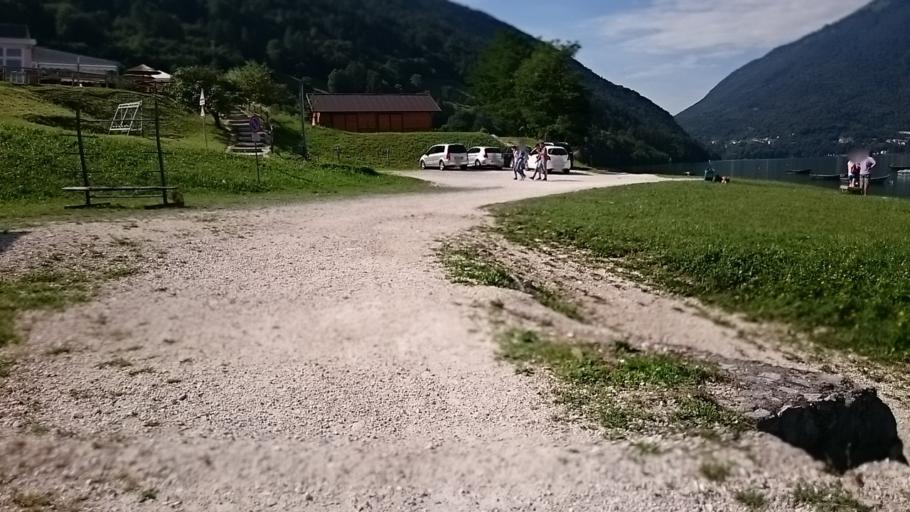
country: IT
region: Veneto
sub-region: Provincia di Belluno
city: Farra d'Alpago
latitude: 46.1077
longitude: 12.3530
